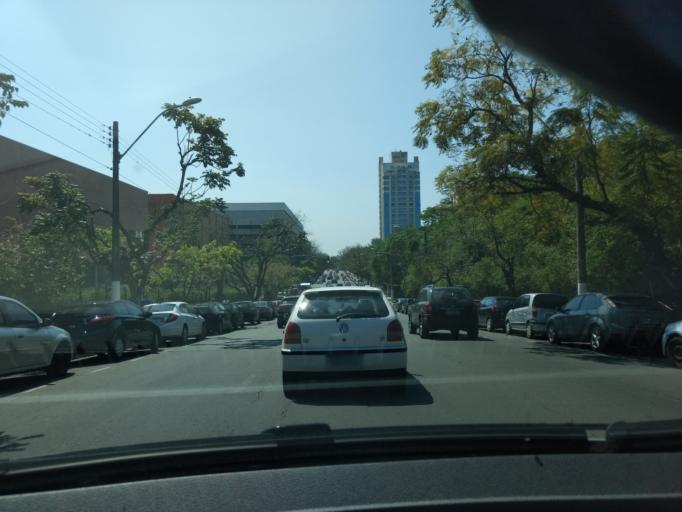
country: BR
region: Rio Grande do Sul
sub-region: Porto Alegre
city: Porto Alegre
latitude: -30.0259
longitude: -51.1612
